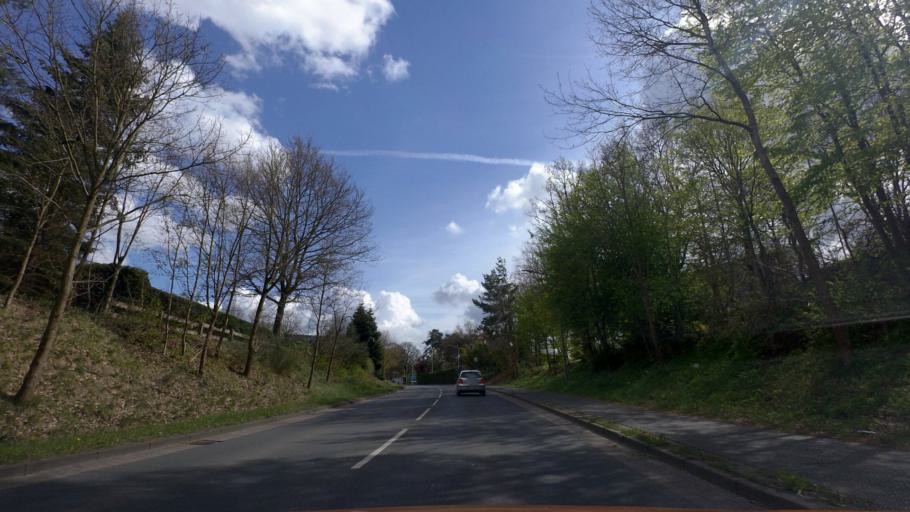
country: DE
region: Lower Saxony
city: Hude
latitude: 53.1027
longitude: 8.4764
